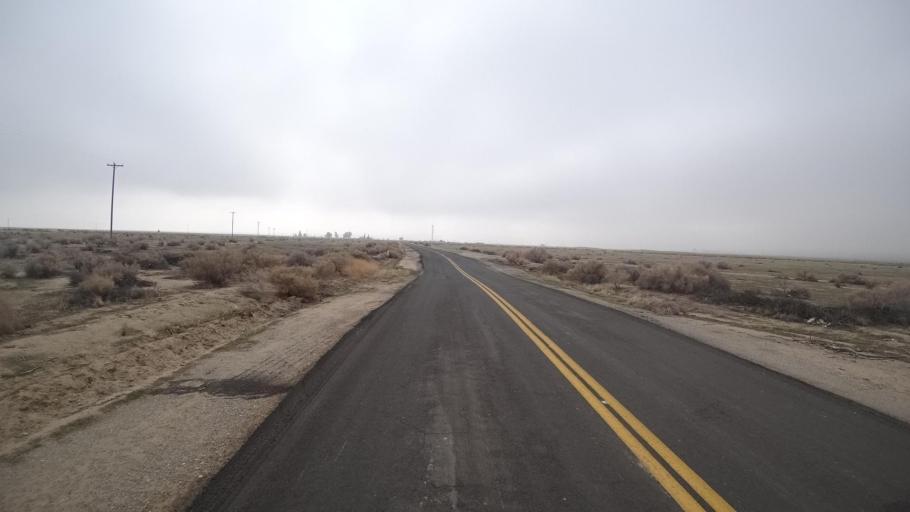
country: US
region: California
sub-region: Kern County
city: Maricopa
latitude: 35.0656
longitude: -119.3496
